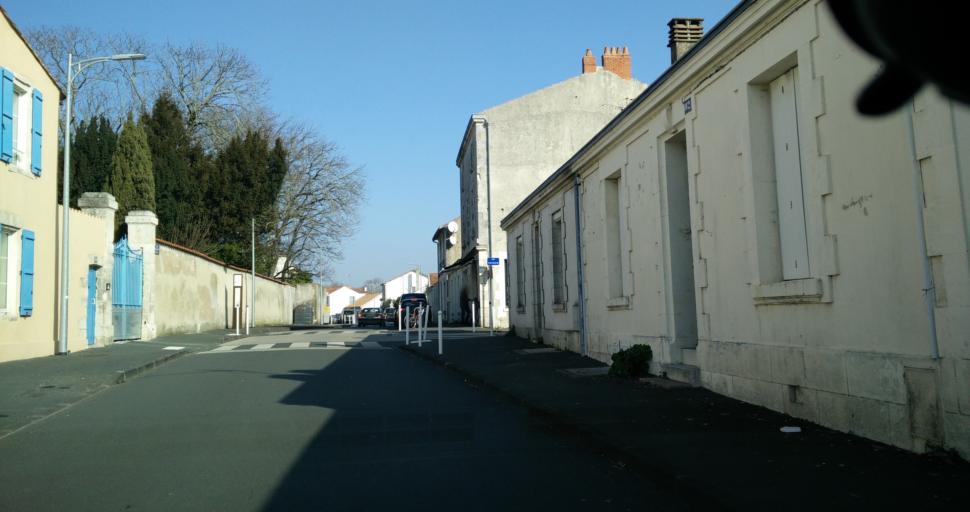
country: FR
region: Poitou-Charentes
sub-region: Departement de la Charente-Maritime
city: La Rochelle
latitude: 46.1683
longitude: -1.1589
